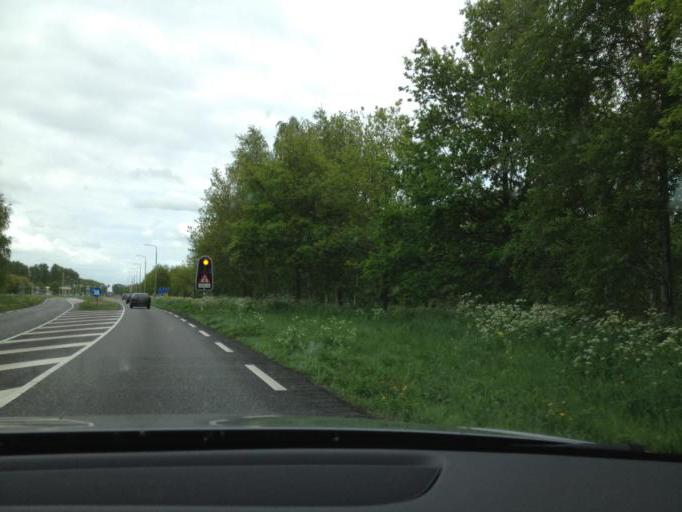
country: NL
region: North Holland
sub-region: Gemeente Huizen
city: Huizen
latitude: 52.3304
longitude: 5.2891
